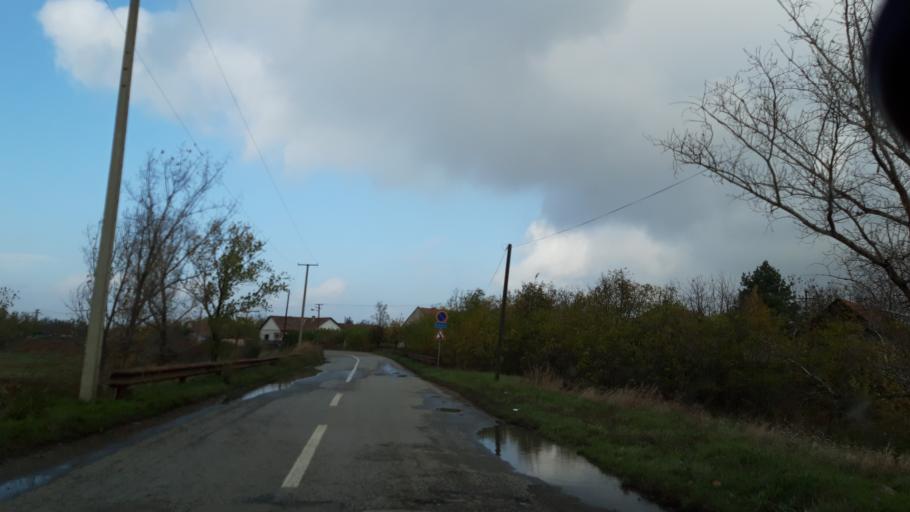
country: RS
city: Padej
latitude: 45.8191
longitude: 20.1586
